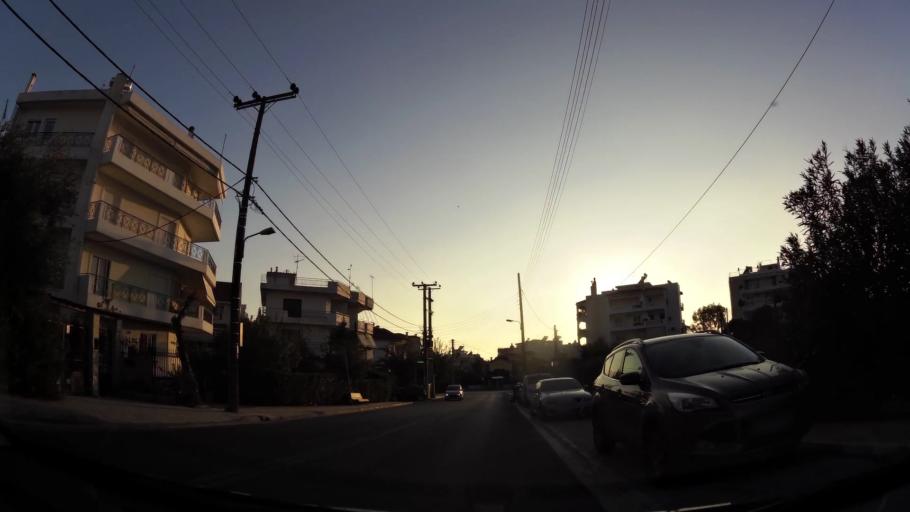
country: GR
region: Attica
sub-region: Nomarchia Athinas
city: Glyfada
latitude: 37.8802
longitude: 23.7672
